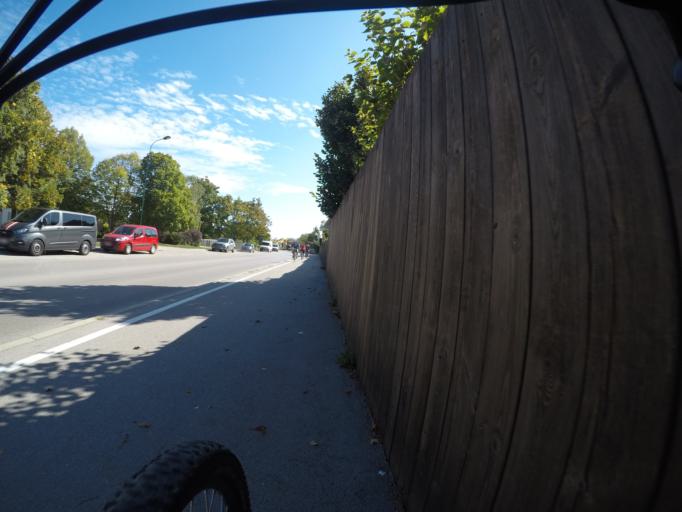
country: AT
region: Lower Austria
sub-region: Politischer Bezirk Modling
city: Wiener Neudorf
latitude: 48.0901
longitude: 16.3034
